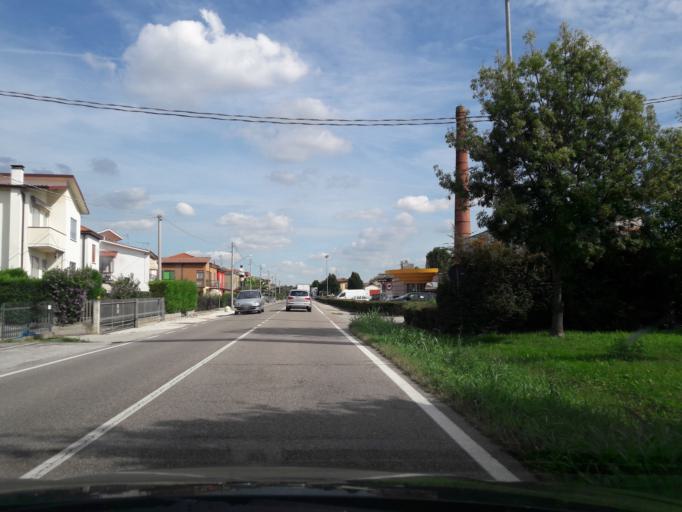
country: IT
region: Veneto
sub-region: Provincia di Rovigo
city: Lendinara
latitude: 45.0882
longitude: 11.5930
